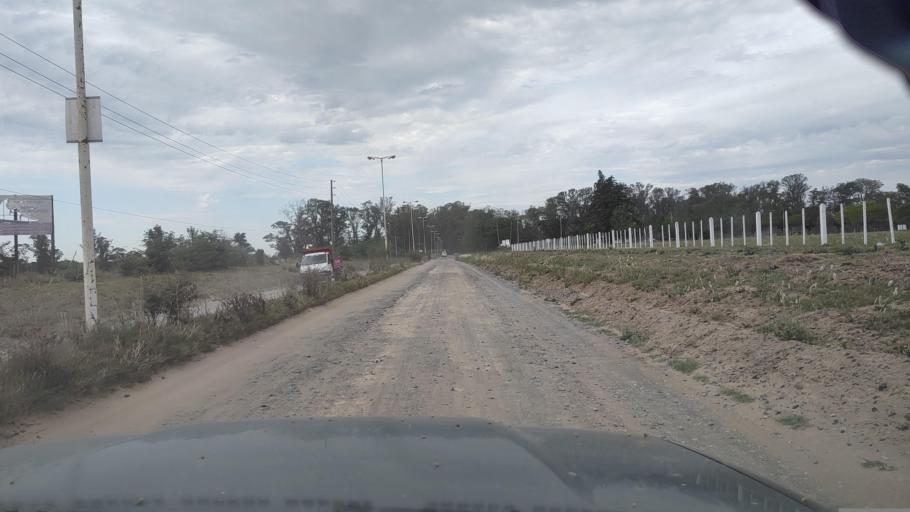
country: AR
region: Buenos Aires
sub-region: Partido de Lujan
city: Lujan
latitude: -34.5471
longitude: -59.0809
